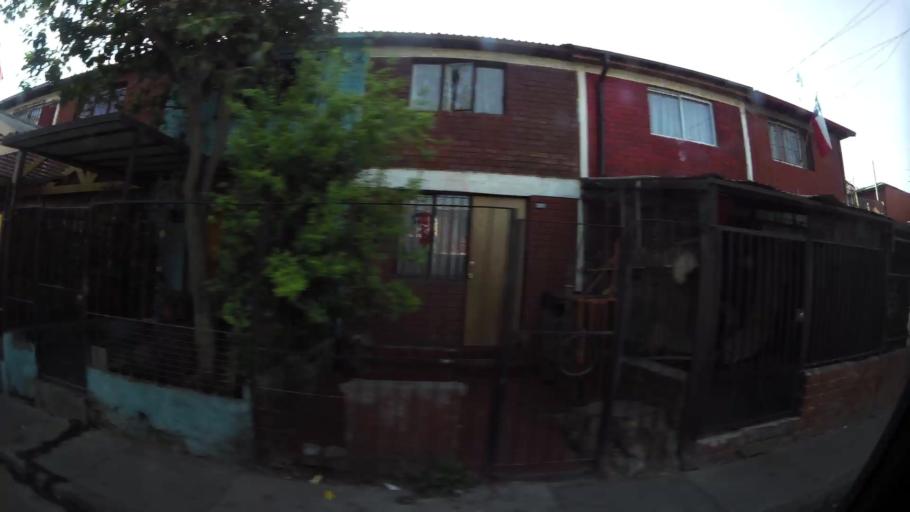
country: CL
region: Santiago Metropolitan
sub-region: Provincia de Santiago
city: Lo Prado
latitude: -33.4154
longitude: -70.7672
